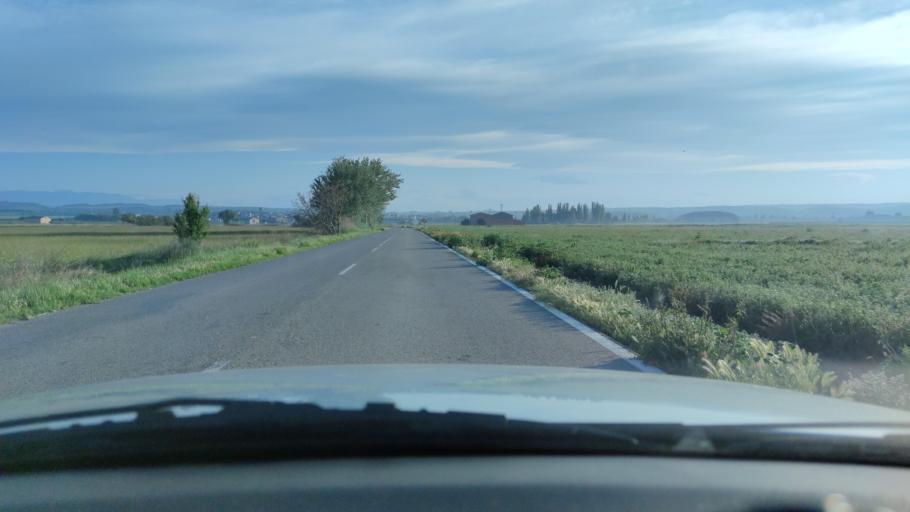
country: ES
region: Catalonia
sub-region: Provincia de Lleida
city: Castellsera
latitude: 41.7336
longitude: 0.9836
